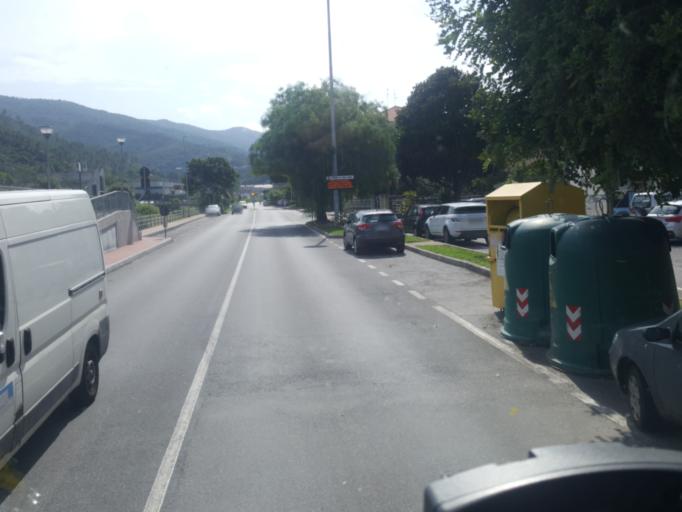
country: IT
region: Liguria
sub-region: Provincia di Savona
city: Valle di Vado
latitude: 44.2629
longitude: 8.4174
